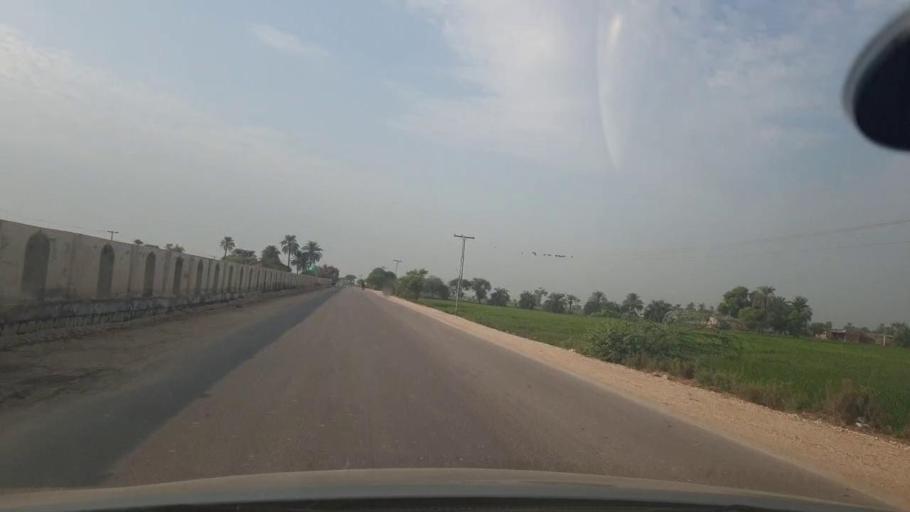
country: PK
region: Sindh
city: Jacobabad
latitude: 28.1949
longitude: 68.3676
